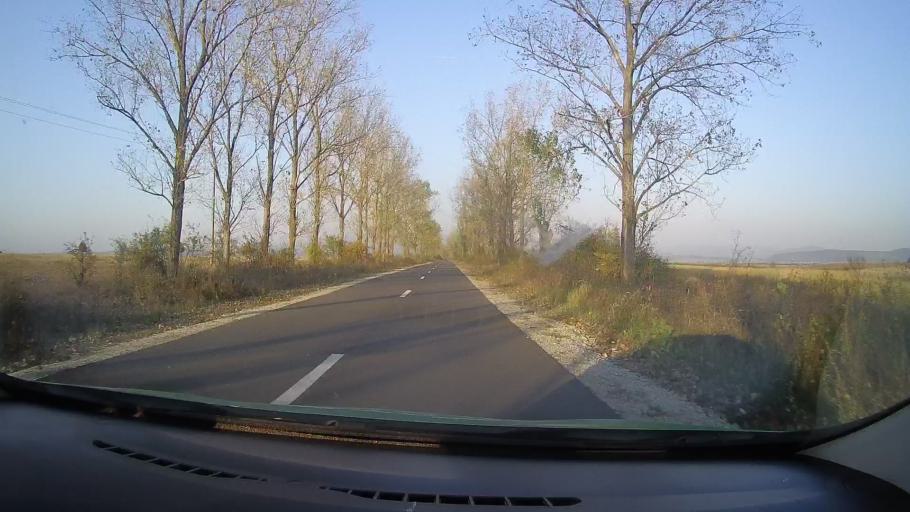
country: RO
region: Arad
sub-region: Comuna Barsa
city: Barsa
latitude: 46.3679
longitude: 22.0412
